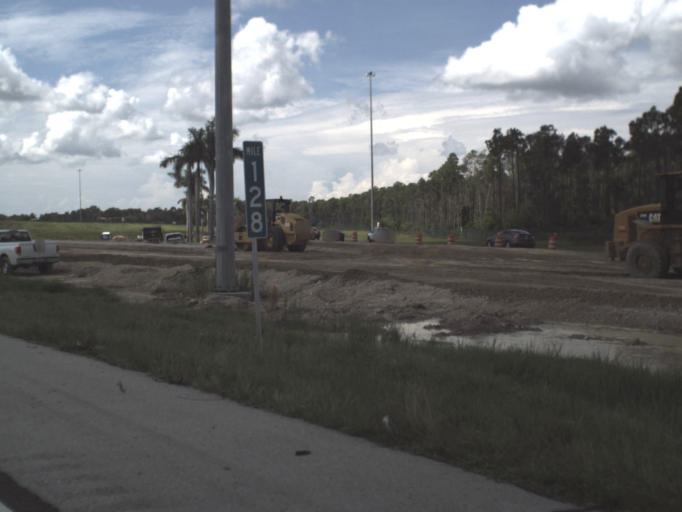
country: US
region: Florida
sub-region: Lee County
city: Three Oaks
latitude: 26.4984
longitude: -81.7947
